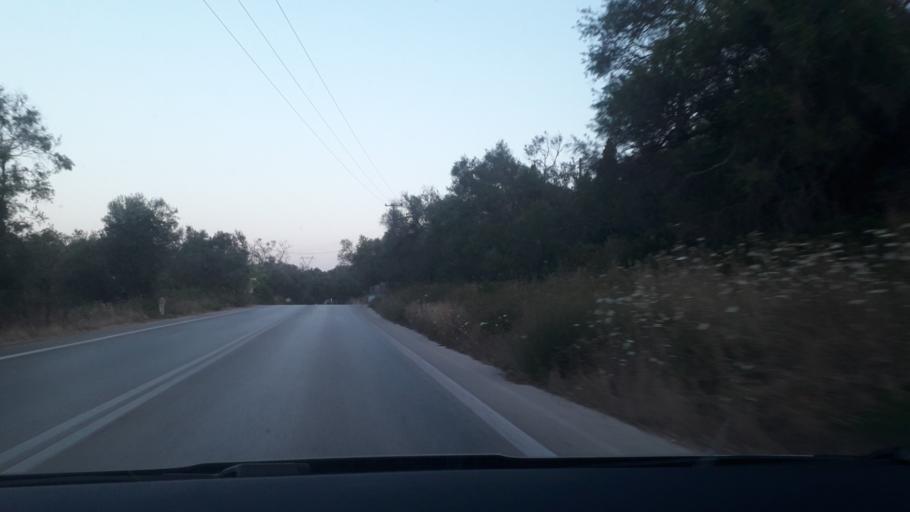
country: GR
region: Ionian Islands
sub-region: Nomos Kerkyras
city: Perivoli
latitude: 39.4431
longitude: 19.9536
